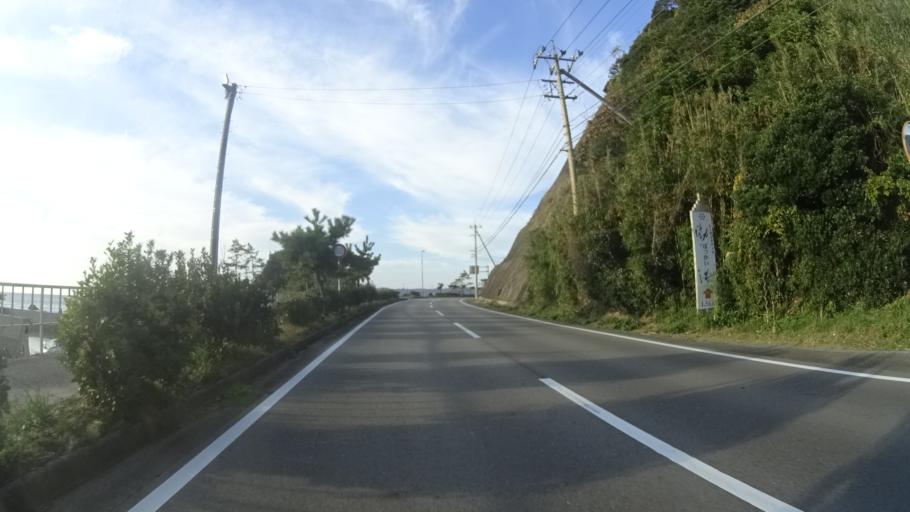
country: JP
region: Ishikawa
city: Hakui
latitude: 37.1281
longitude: 136.7281
